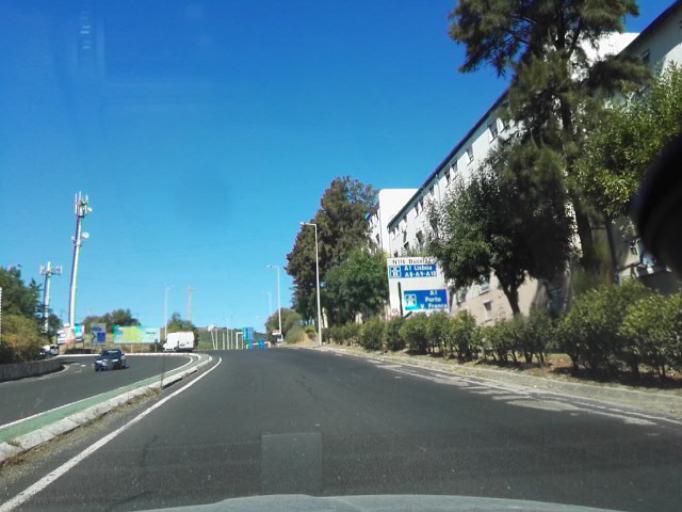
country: PT
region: Lisbon
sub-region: Vila Franca de Xira
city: Vialonga
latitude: 38.8916
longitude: -9.0460
